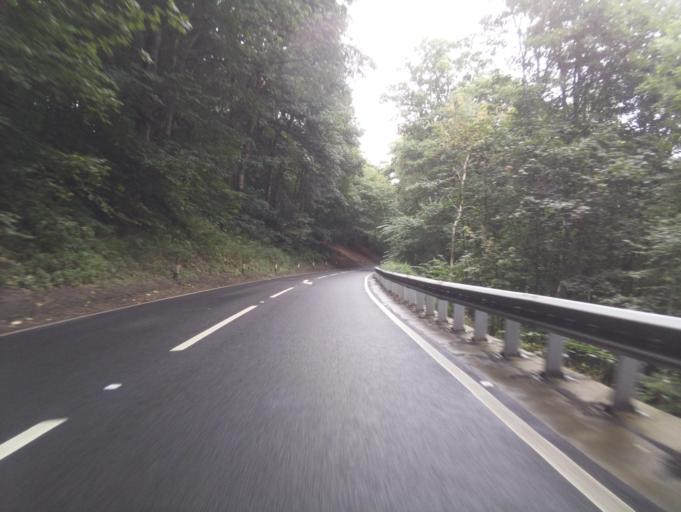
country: GB
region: Scotland
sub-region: The Scottish Borders
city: Jedburgh
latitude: 55.4066
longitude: -2.5057
